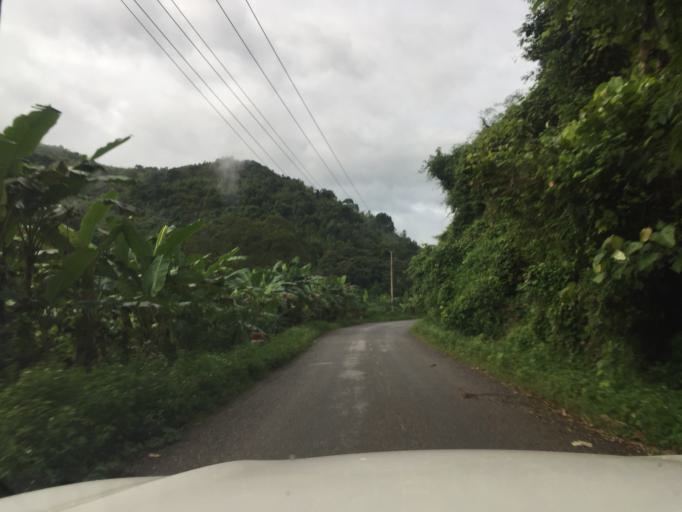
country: LA
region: Phongsali
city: Khoa
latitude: 21.0932
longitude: 102.2468
